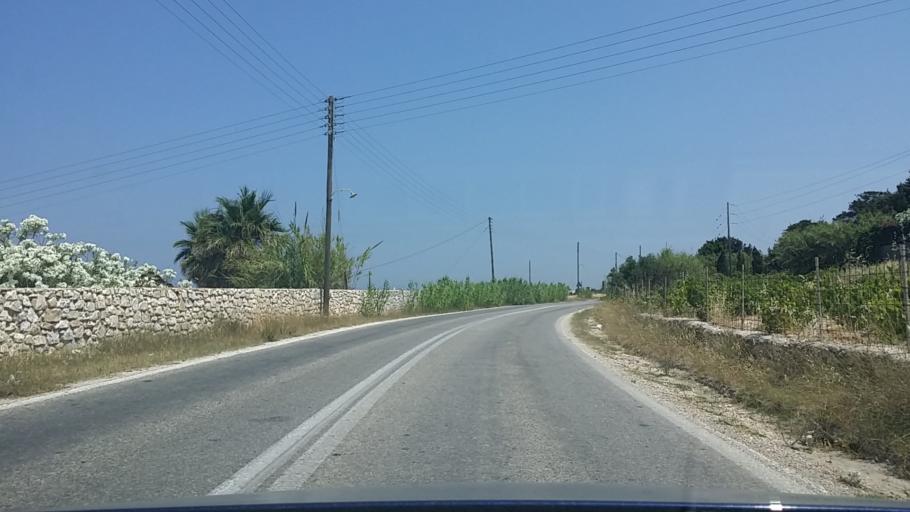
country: GR
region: South Aegean
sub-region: Nomos Kykladon
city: Antiparos
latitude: 37.0577
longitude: 25.1170
